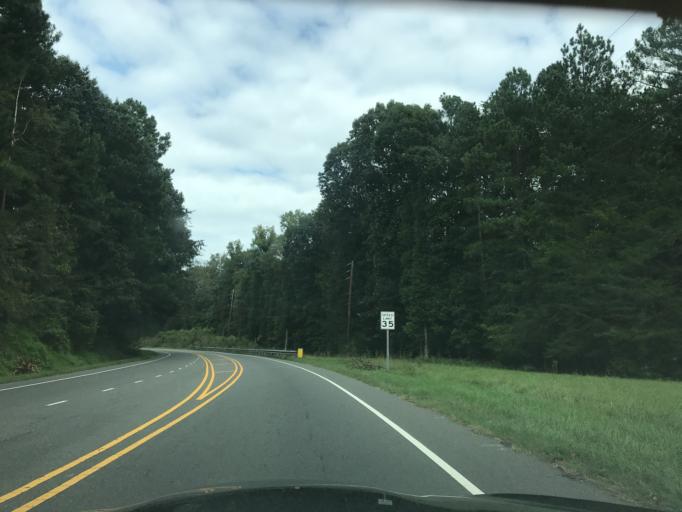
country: US
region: North Carolina
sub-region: Orange County
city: Carrboro
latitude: 35.9250
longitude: -79.0685
